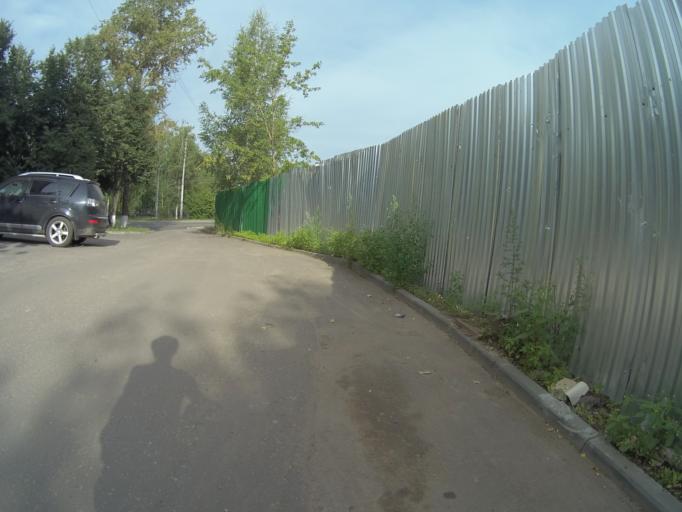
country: RU
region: Vladimir
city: Kommunar
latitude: 56.1466
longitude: 40.4345
